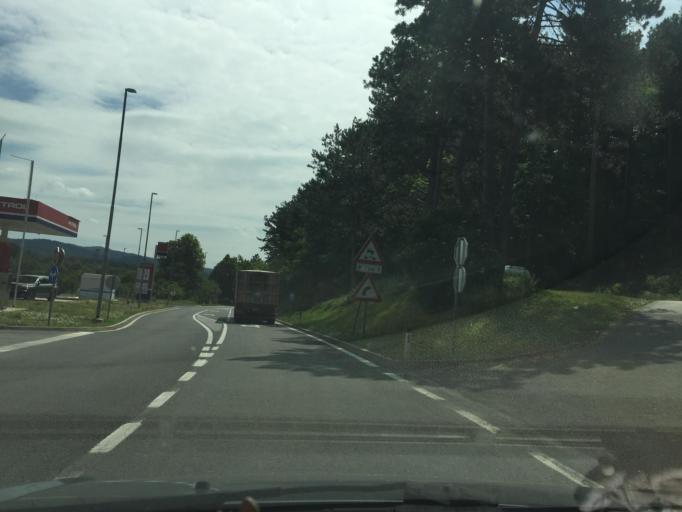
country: SI
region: Hrpelje-Kozina
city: Kozina
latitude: 45.6043
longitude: 13.9494
